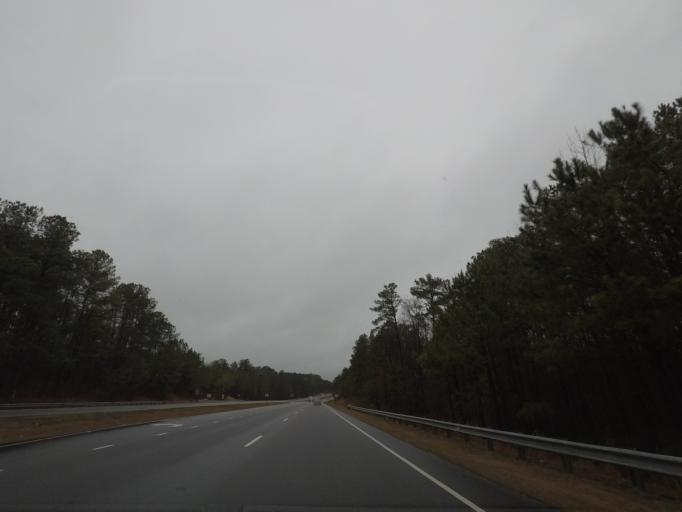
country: US
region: North Carolina
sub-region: Lee County
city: Broadway
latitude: 35.3247
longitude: -79.0925
